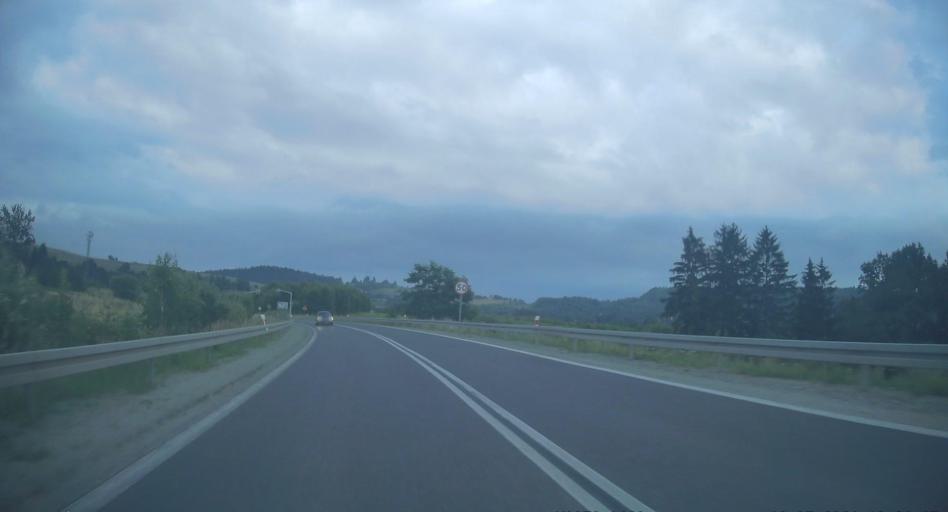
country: PL
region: Lower Silesian Voivodeship
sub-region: Powiat klodzki
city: Nowa Ruda
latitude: 50.5987
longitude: 16.5135
